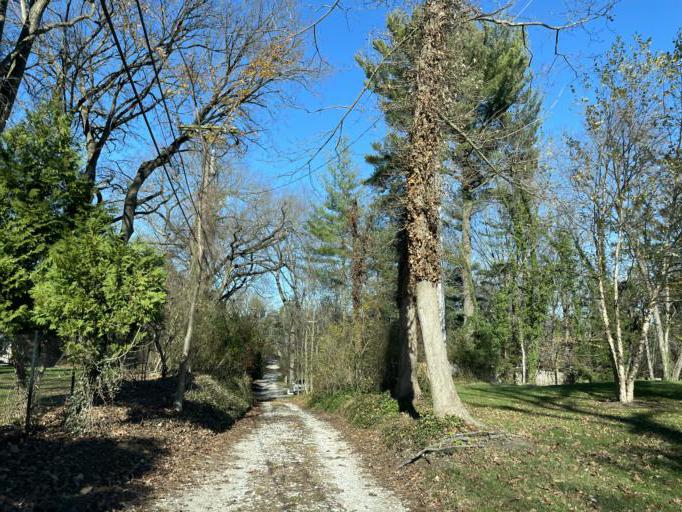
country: US
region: Maryland
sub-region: Baltimore County
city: Mays Chapel
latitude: 39.4074
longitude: -76.6548
